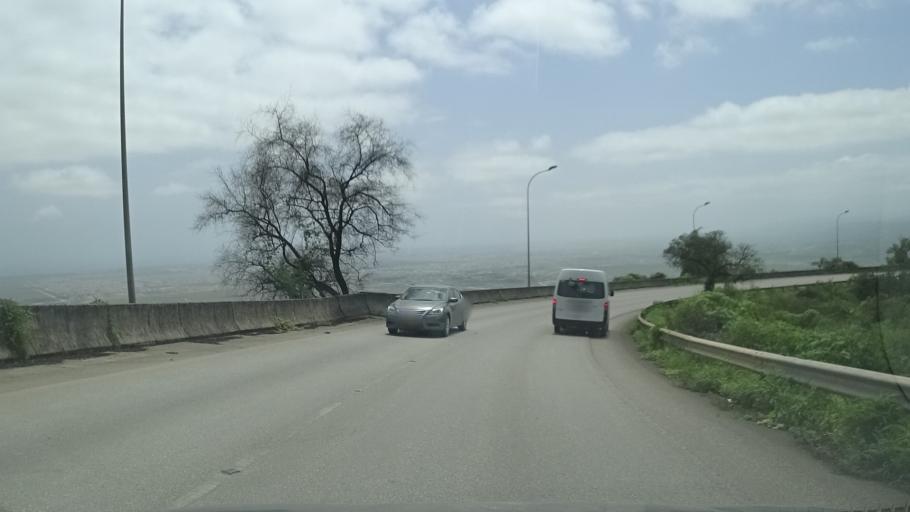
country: OM
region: Zufar
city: Salalah
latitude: 17.1521
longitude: 54.2227
